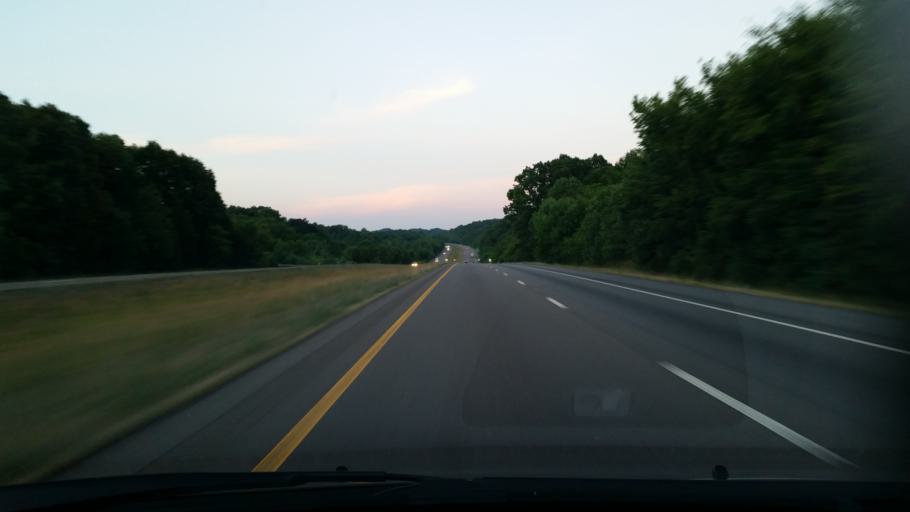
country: US
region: Tennessee
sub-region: Washington County
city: Fall Branch
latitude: 36.3546
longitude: -82.7318
